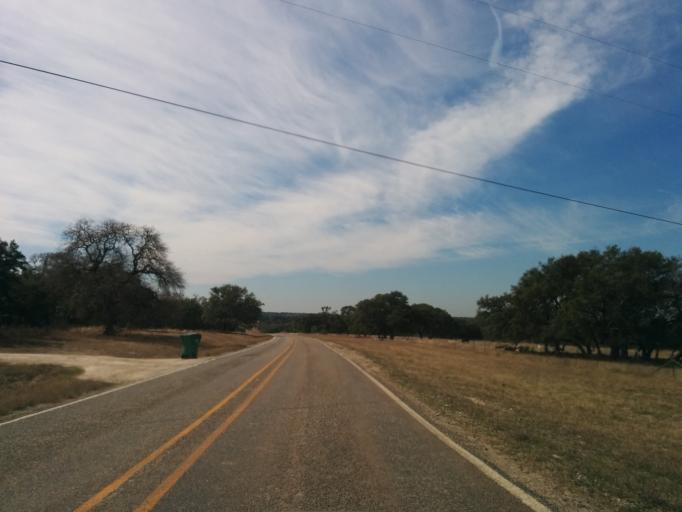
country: US
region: Texas
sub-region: Blanco County
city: Blanco
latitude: 29.9646
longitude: -98.5333
